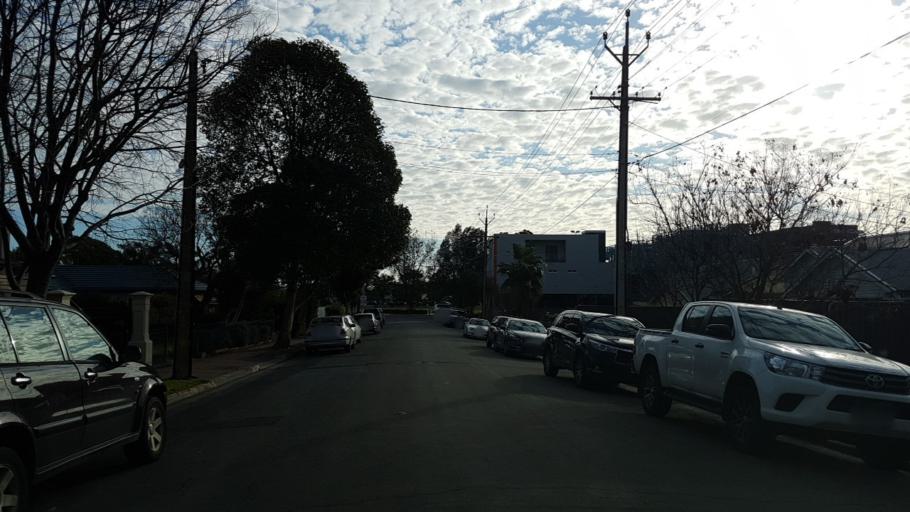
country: AU
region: South Australia
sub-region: Prospect
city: Prospect
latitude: -34.8886
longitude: 138.5864
